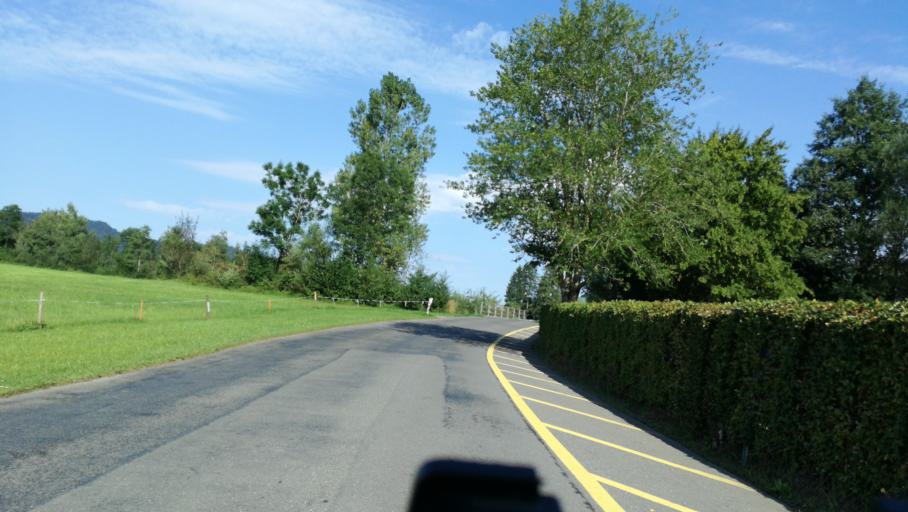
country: CH
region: Zug
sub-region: Zug
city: Unterageri
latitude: 47.1279
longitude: 8.5901
